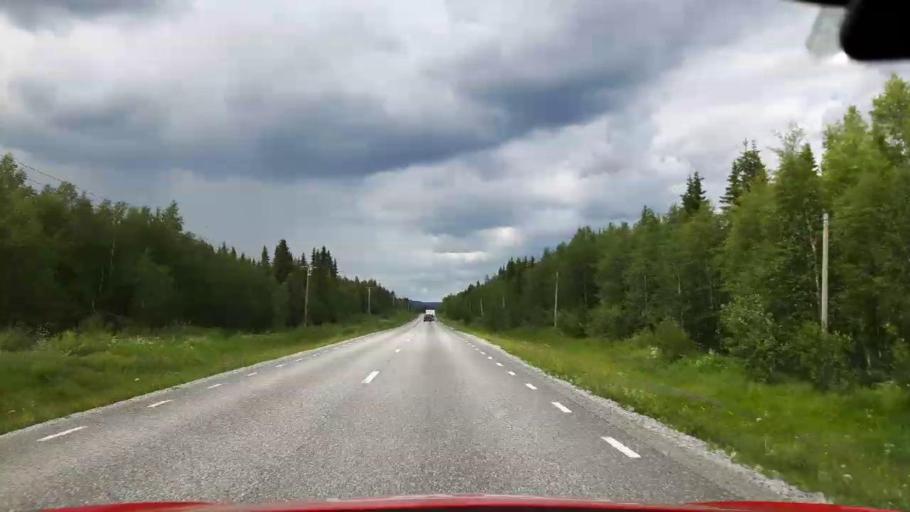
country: SE
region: Jaemtland
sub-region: Krokoms Kommun
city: Krokom
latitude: 63.6640
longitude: 14.3587
